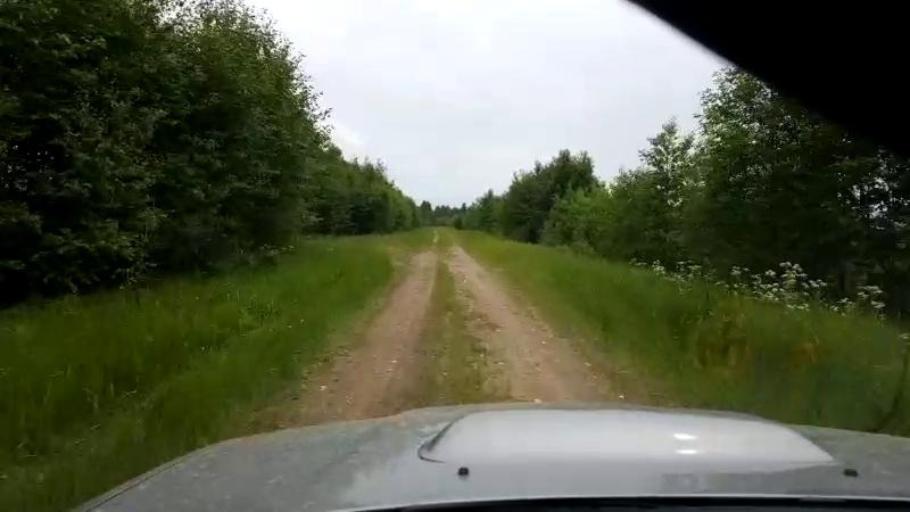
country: EE
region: Paernumaa
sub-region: Tootsi vald
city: Tootsi
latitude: 58.5591
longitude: 24.6880
